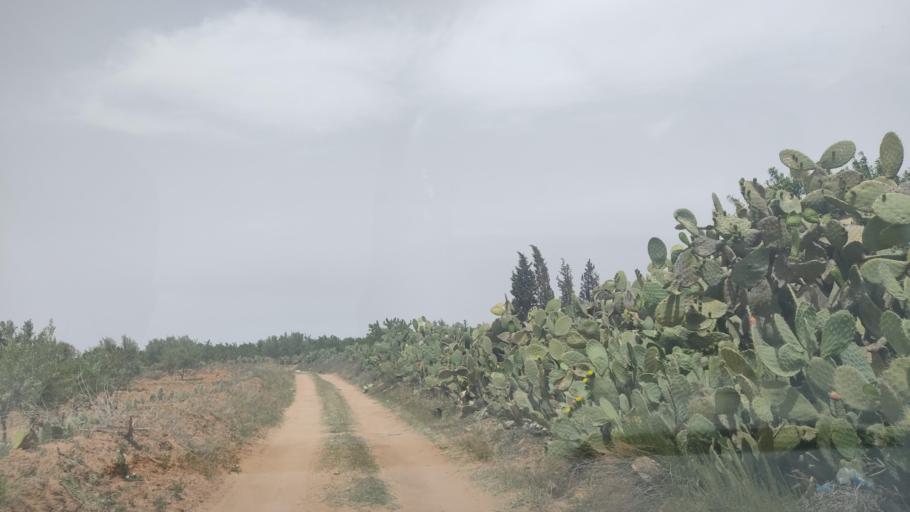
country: TN
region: Safaqis
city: Sfax
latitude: 34.8434
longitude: 10.5917
